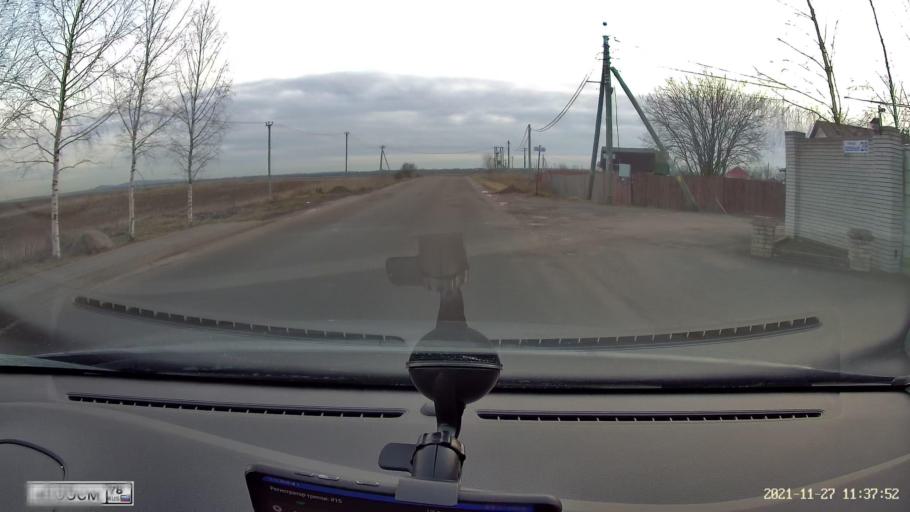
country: RU
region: Leningrad
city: Russko-Vysotskoye
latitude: 59.6922
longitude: 29.9925
